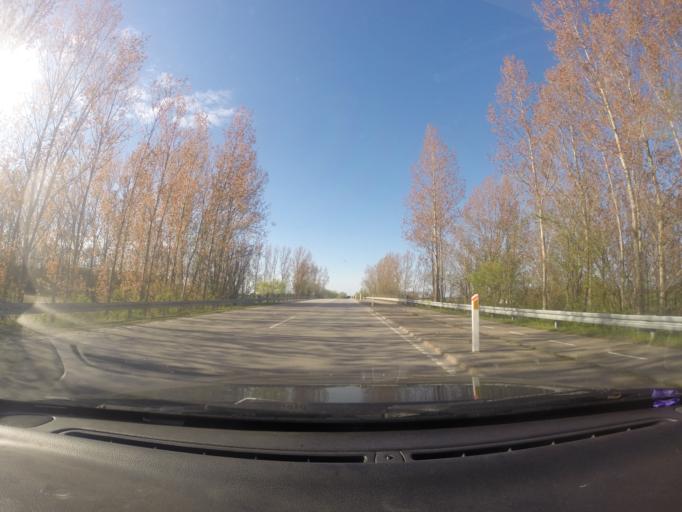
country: DK
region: Capital Region
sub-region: Hoje-Taastrup Kommune
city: Taastrup
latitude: 55.6646
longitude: 12.2543
